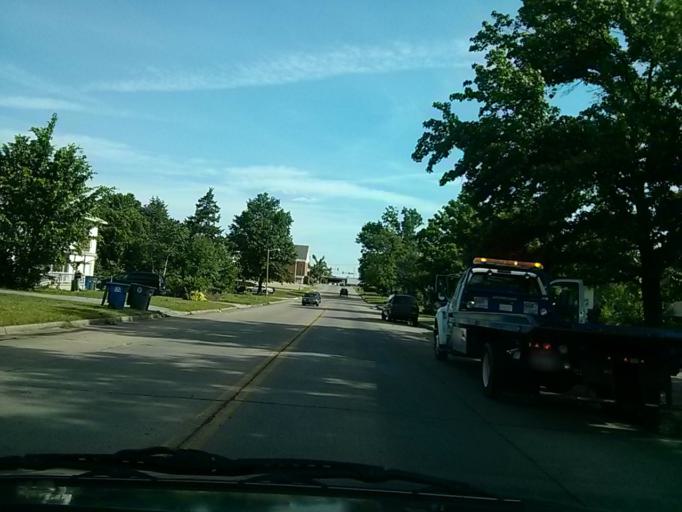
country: US
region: Oklahoma
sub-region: Tulsa County
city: Tulsa
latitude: 36.1581
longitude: -95.8956
